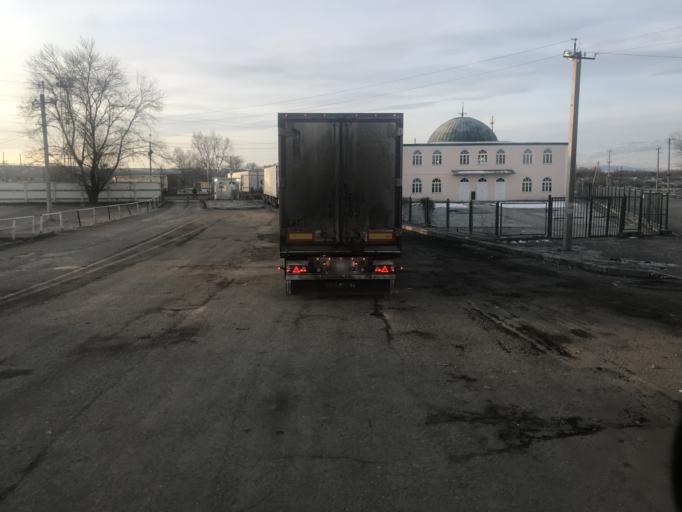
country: AZ
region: Qusar
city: Samur
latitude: 41.6423
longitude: 48.4050
